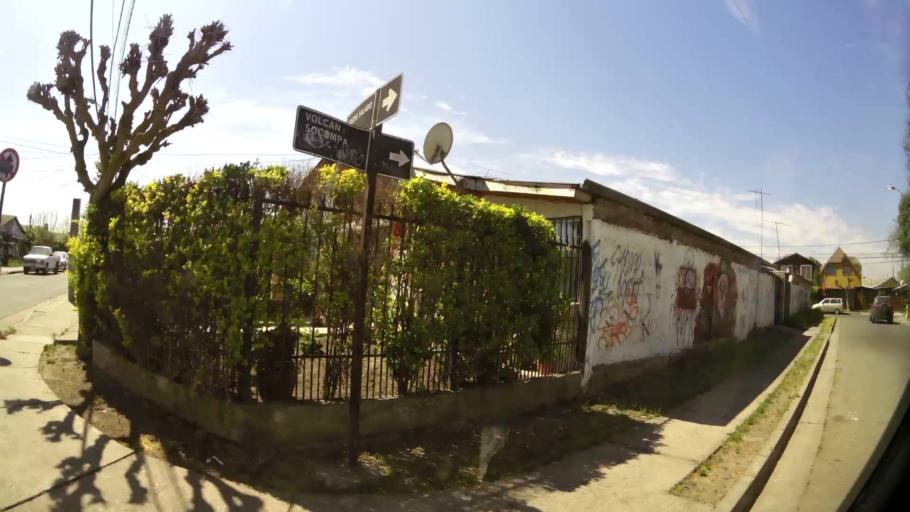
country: CL
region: Santiago Metropolitan
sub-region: Provincia de Talagante
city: Talagante
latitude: -33.6560
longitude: -70.9111
